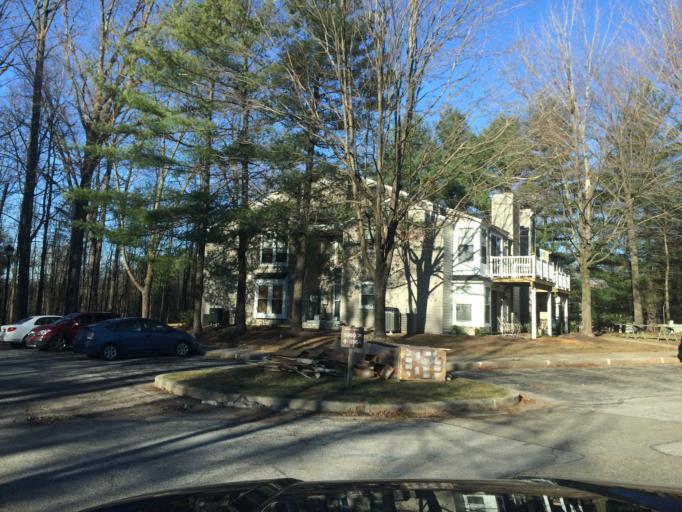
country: US
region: Maryland
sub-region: Howard County
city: Riverside
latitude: 39.2079
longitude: -76.8933
